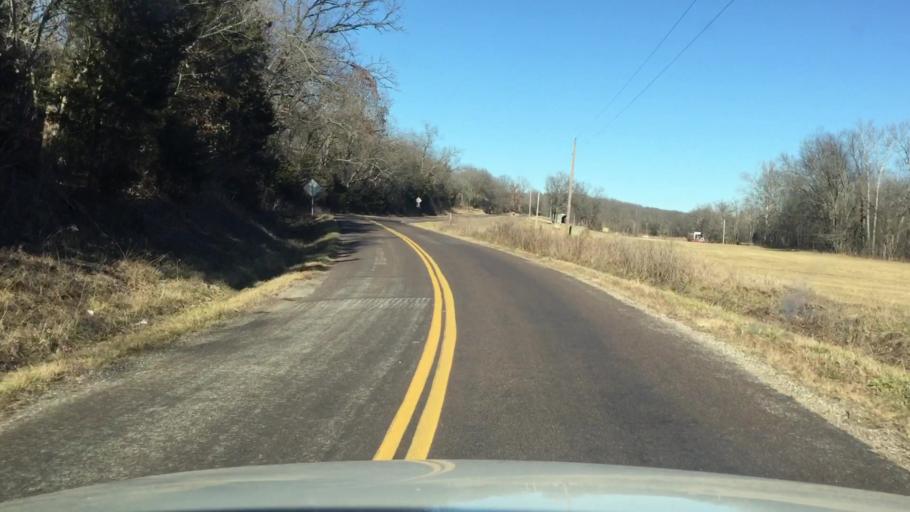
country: US
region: Missouri
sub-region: Miller County
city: Eldon
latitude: 38.3419
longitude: -92.7082
